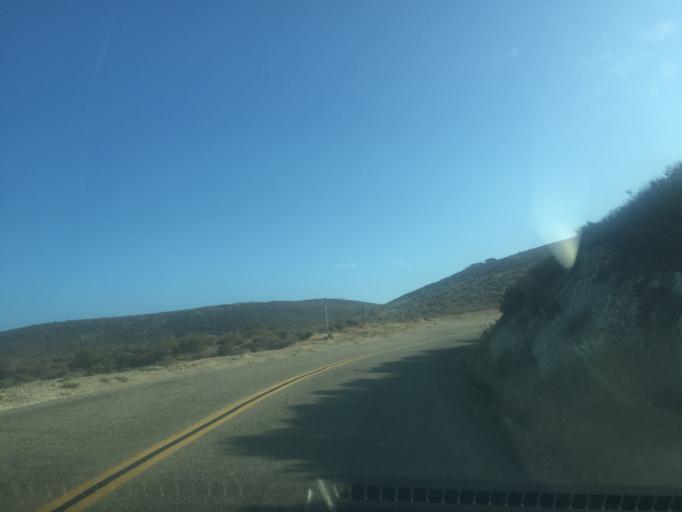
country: US
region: California
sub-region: Santa Barbara County
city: Lompoc
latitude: 34.5104
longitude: -120.4985
